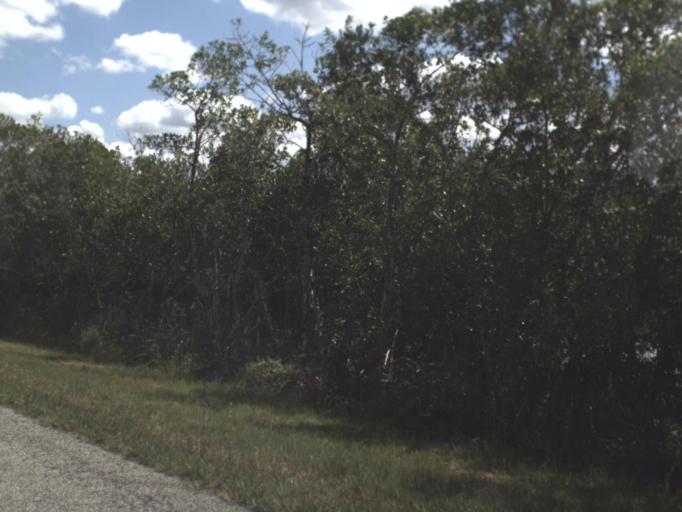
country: US
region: Florida
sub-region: Collier County
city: Marco
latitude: 25.9124
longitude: -81.3682
